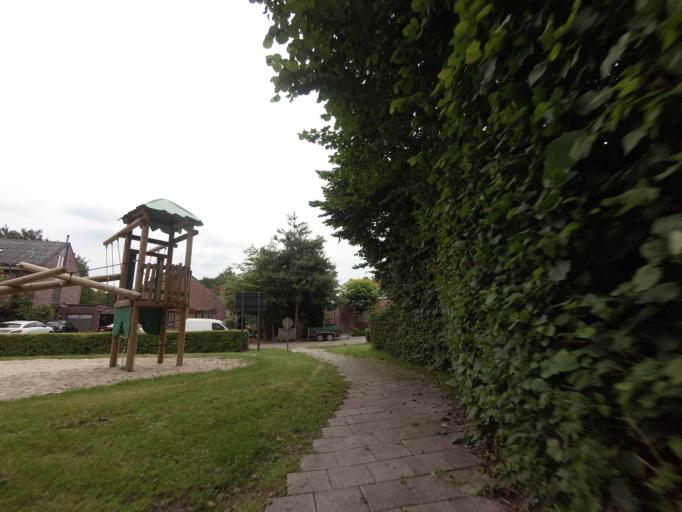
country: BE
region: Flanders
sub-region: Provincie Antwerpen
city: Schilde
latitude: 51.2405
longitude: 4.5942
